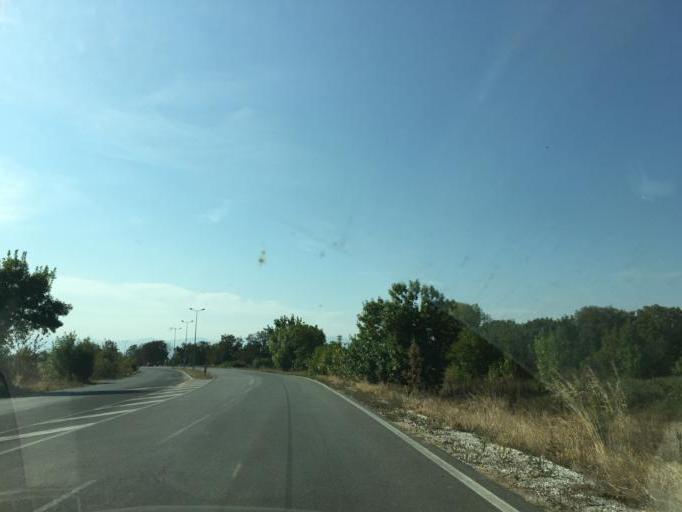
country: BG
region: Pazardzhik
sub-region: Obshtina Pazardzhik
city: Pazardzhik
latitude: 42.2241
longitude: 24.3102
